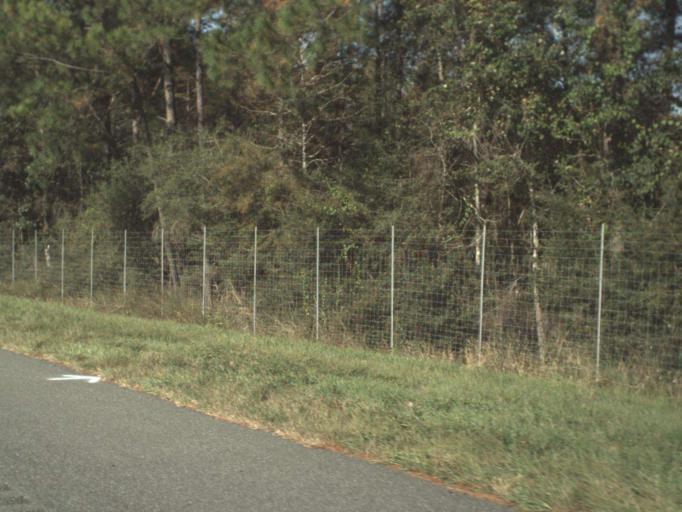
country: US
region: Florida
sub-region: Holmes County
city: Bonifay
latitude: 30.7424
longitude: -85.8757
